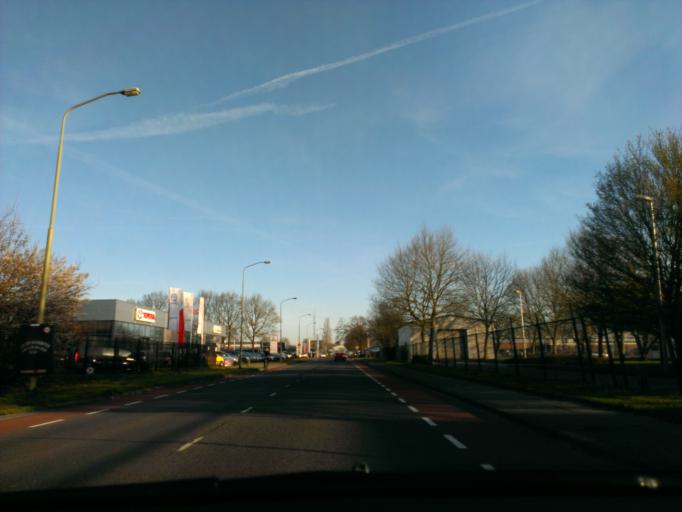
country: NL
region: Drenthe
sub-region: Gemeente Emmen
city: Emmen
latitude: 52.7686
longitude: 6.9250
